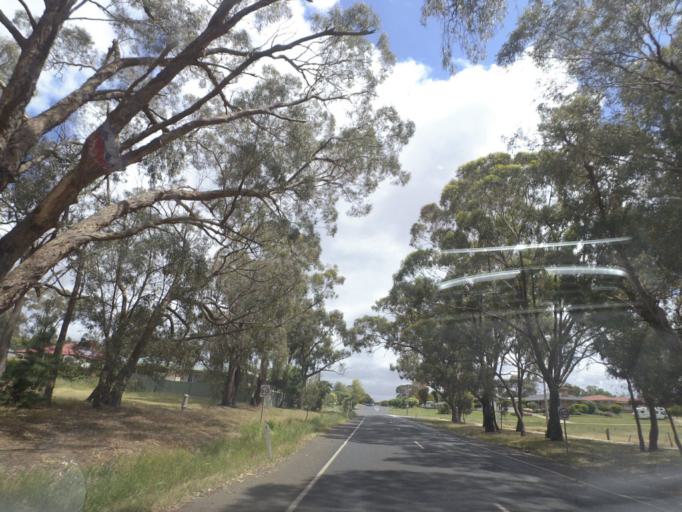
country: AU
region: Victoria
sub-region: Whittlesea
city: Whittlesea
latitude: -37.2113
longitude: 145.0472
